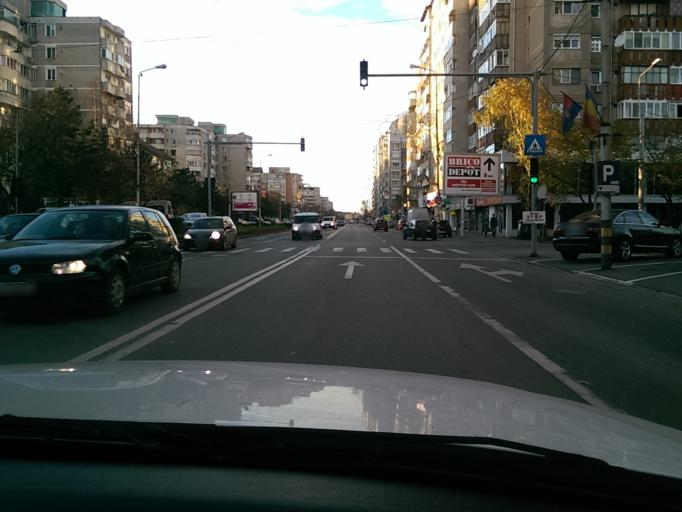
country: RO
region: Bihor
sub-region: Comuna Sanmartin
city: Sanmartin
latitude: 47.0312
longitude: 21.9531
